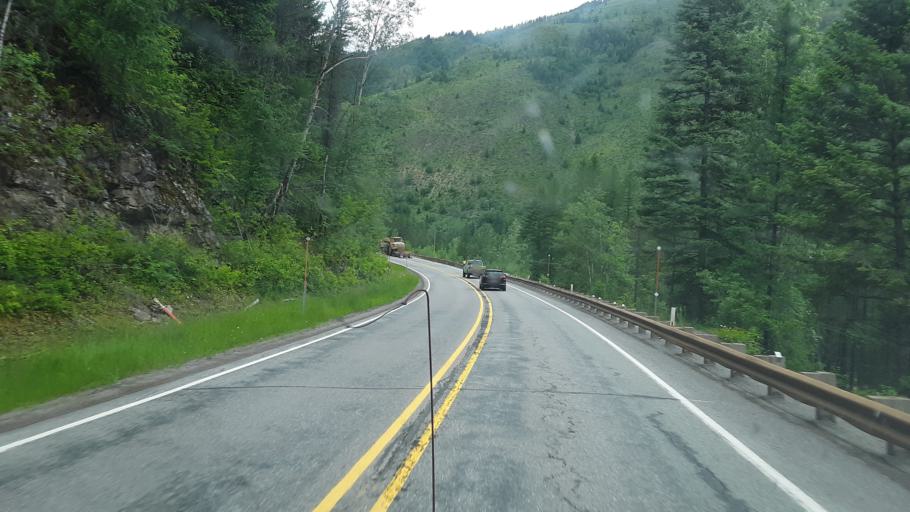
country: US
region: Montana
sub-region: Flathead County
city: Columbia Falls
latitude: 48.4934
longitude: -113.8820
